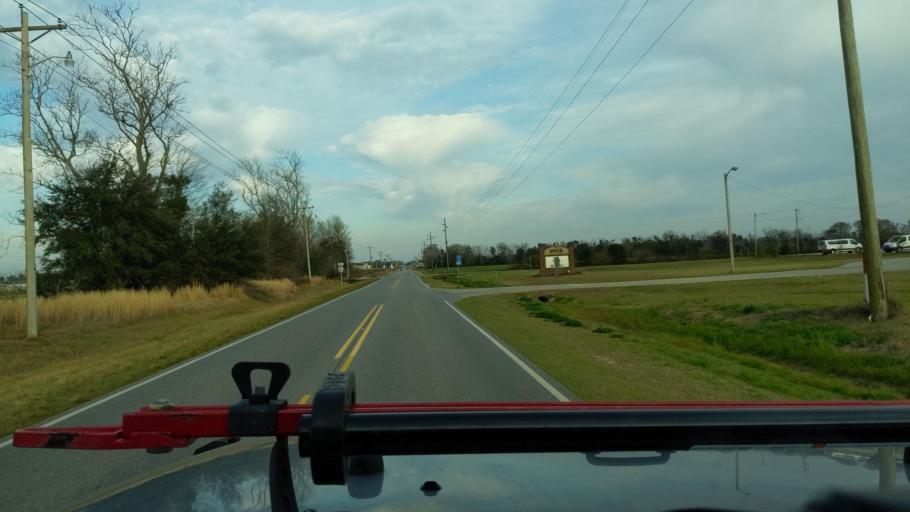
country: US
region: Alabama
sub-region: Baldwin County
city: Foley
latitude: 30.4581
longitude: -87.7017
